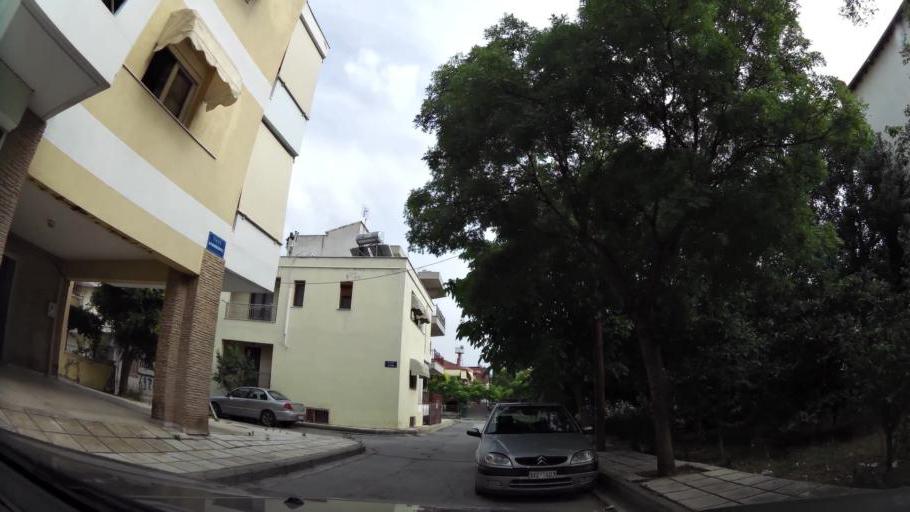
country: GR
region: Central Macedonia
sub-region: Nomos Thessalonikis
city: Stavroupoli
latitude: 40.6823
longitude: 22.9364
